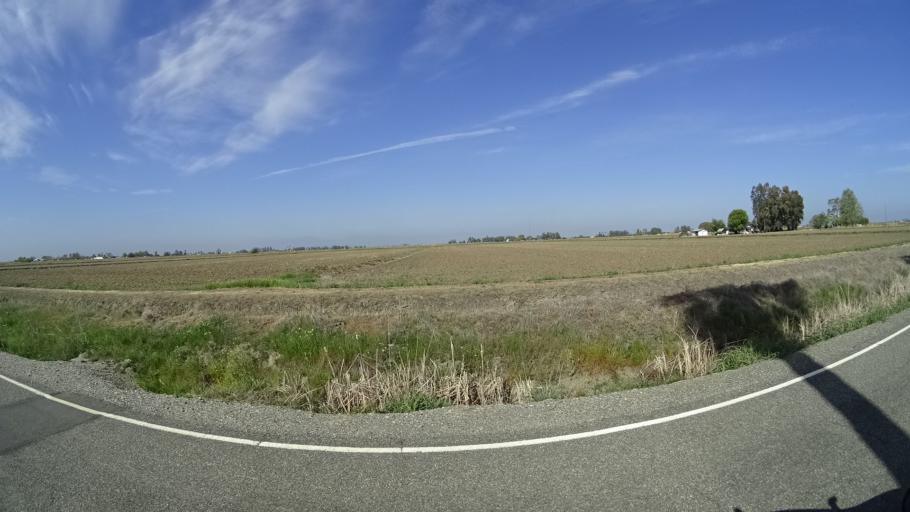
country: US
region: California
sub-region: Glenn County
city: Hamilton City
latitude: 39.5926
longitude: -122.0368
